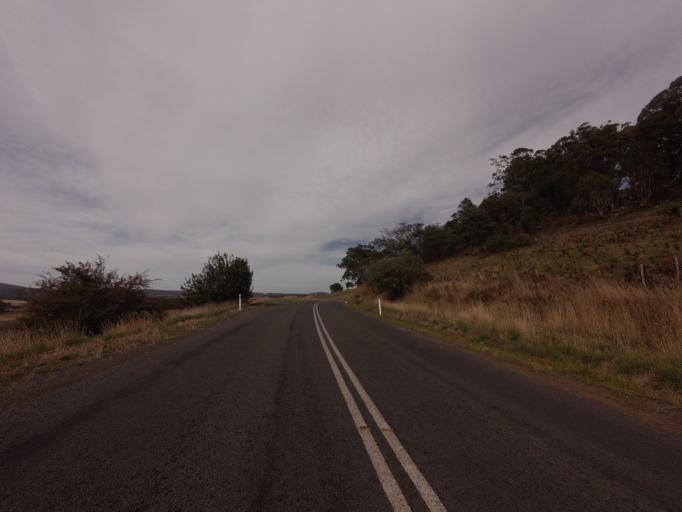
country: AU
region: Tasmania
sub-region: Sorell
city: Sorell
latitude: -42.4209
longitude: 147.4652
